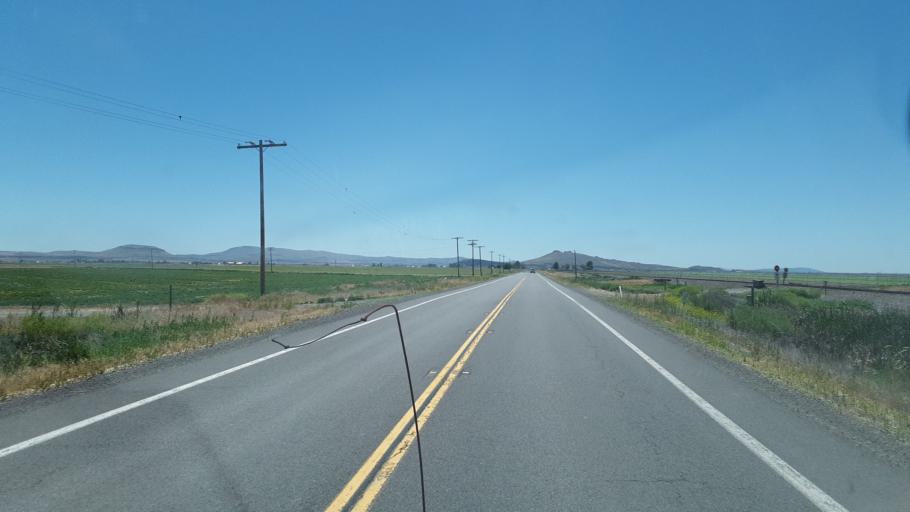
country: US
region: California
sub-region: Siskiyou County
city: Tulelake
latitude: 41.9381
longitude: -121.4517
